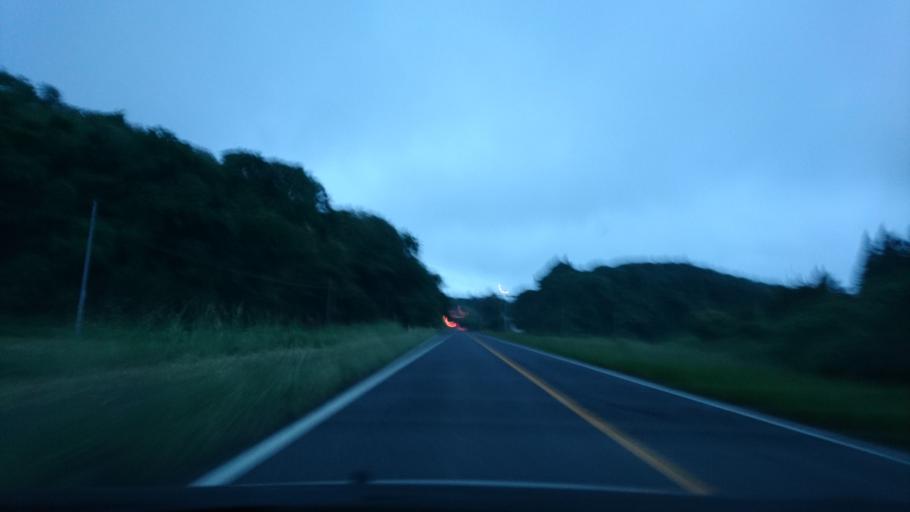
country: JP
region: Iwate
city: Ichinoseki
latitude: 38.8611
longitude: 141.1042
